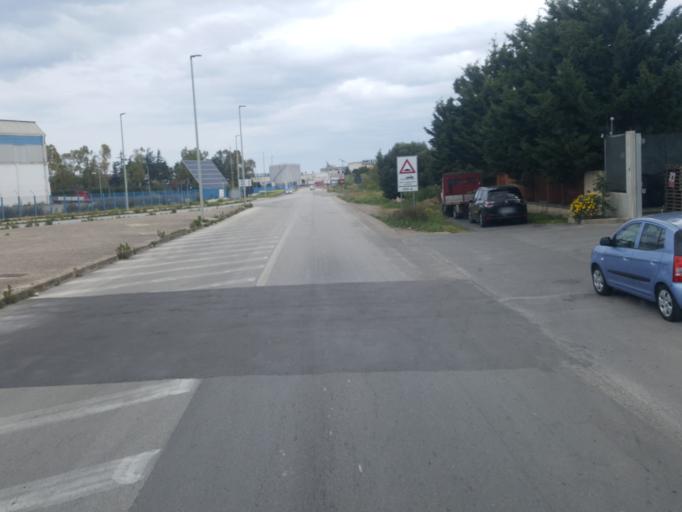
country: IT
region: Apulia
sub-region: Provincia di Bari
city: Modugno
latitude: 41.1011
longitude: 16.7910
